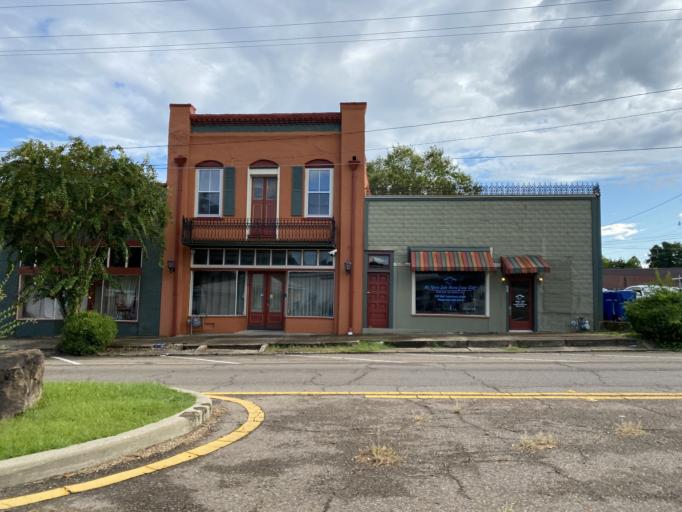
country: US
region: Mississippi
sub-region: Monroe County
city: Aberdeen
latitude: 33.8246
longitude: -88.5405
